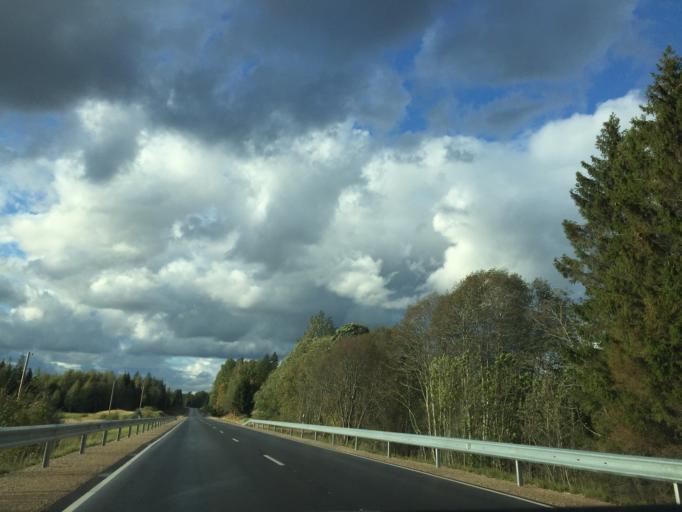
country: LV
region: Ligatne
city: Ligatne
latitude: 57.1461
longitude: 25.0767
